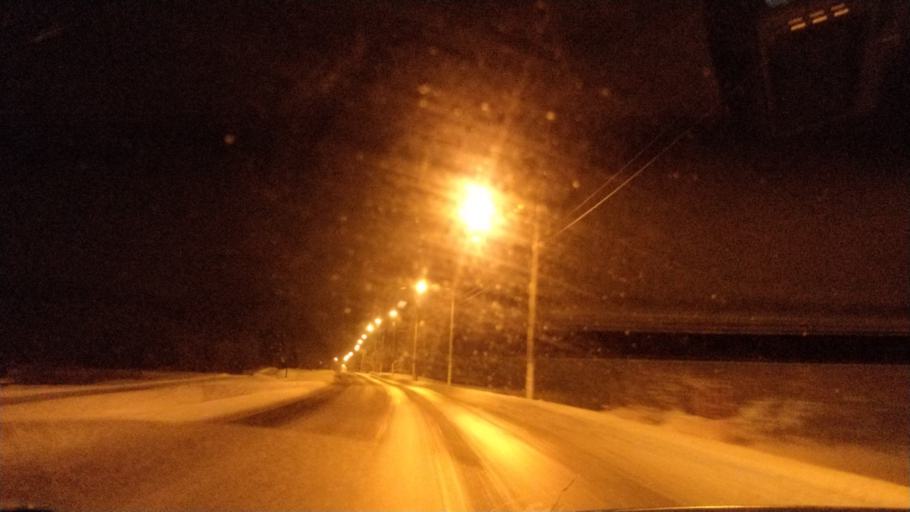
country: FI
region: Lapland
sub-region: Rovaniemi
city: Rovaniemi
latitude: 66.2675
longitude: 25.3327
